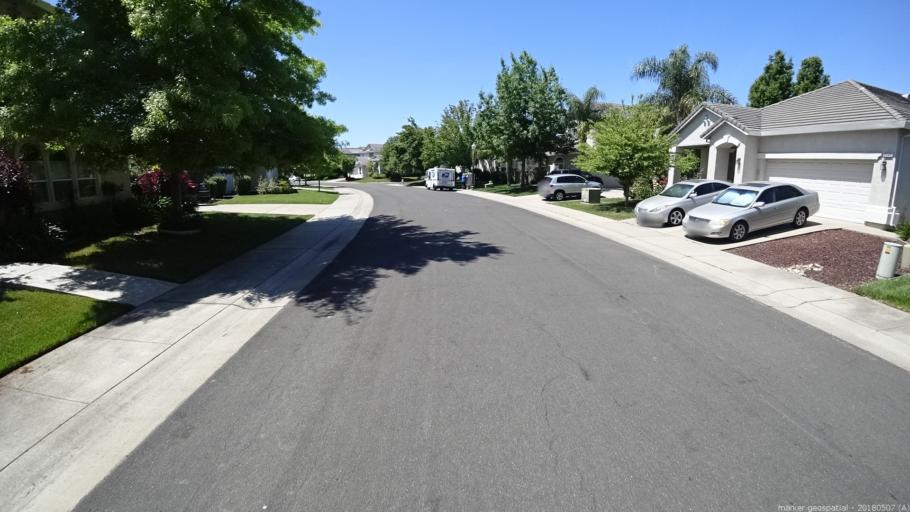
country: US
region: California
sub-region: Sacramento County
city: Elverta
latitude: 38.6776
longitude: -121.5168
